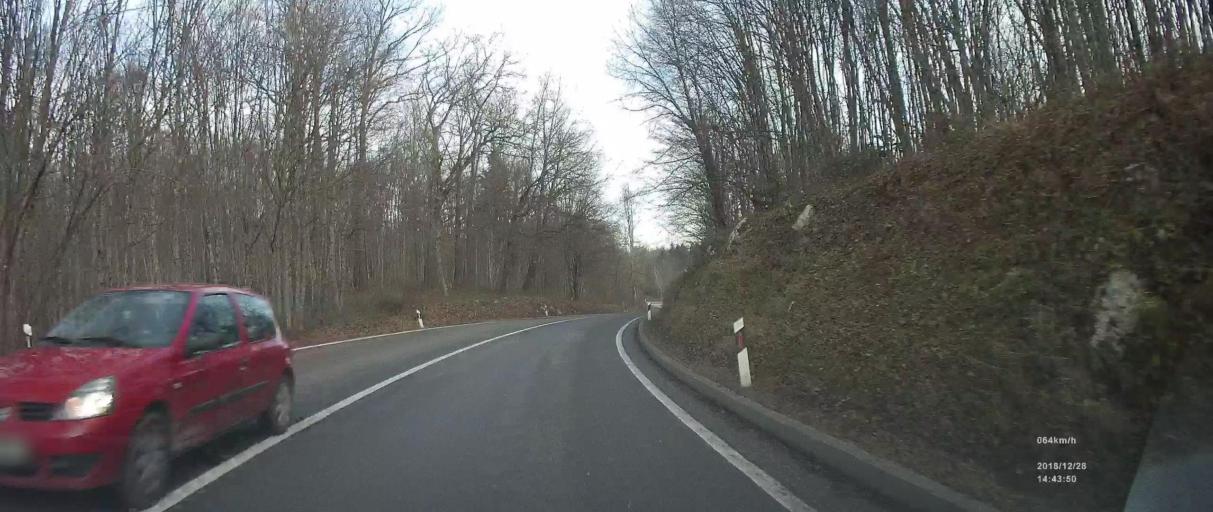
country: SI
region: Crnomelj
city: Crnomelj
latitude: 45.4481
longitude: 15.2835
